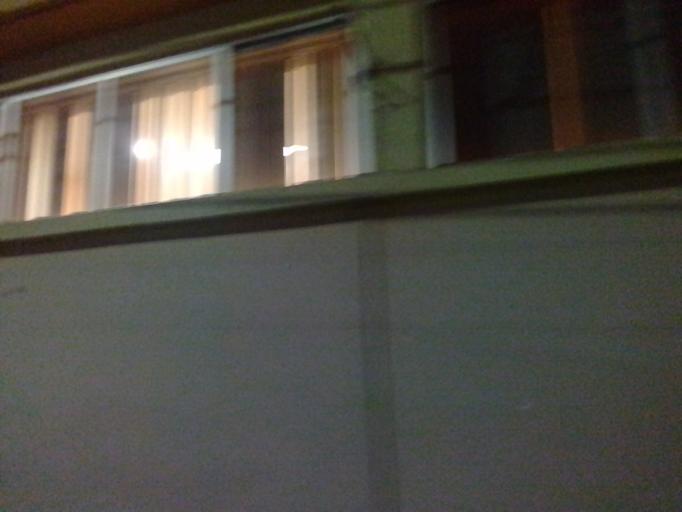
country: MX
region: Oaxaca
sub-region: Salina Cruz
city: Salina Cruz
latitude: 16.1820
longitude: -95.1951
